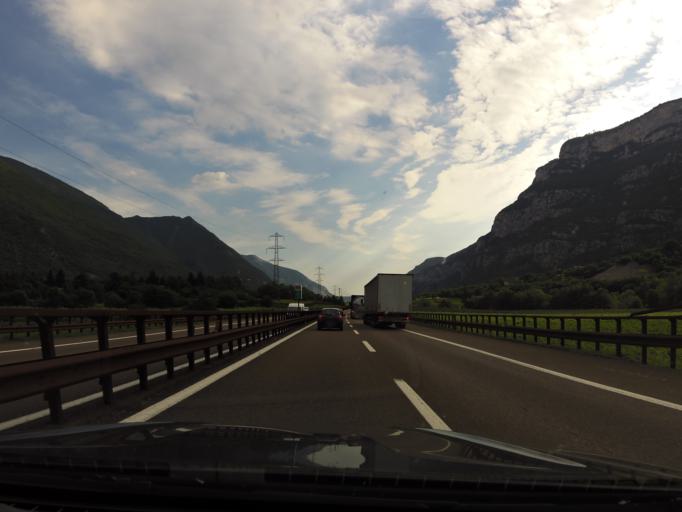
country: IT
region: Veneto
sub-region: Provincia di Verona
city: Rivalta
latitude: 45.6469
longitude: 10.8843
